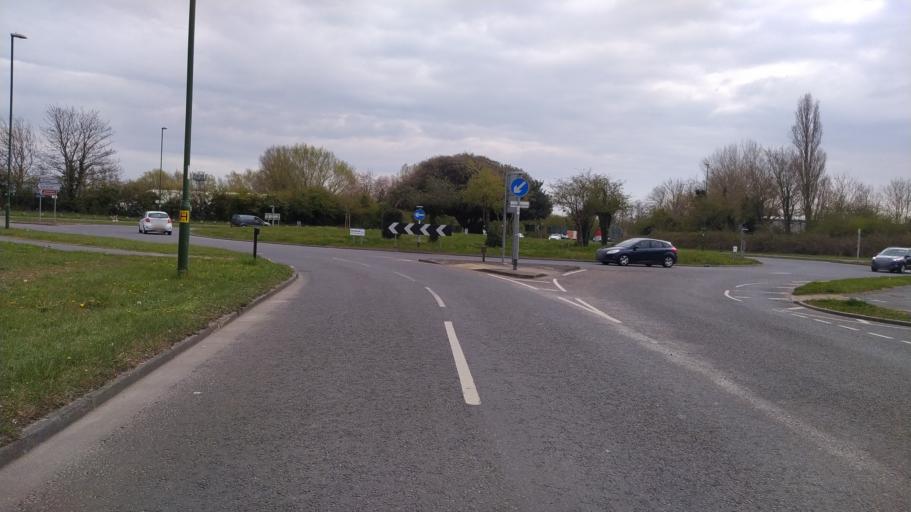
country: GB
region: England
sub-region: West Sussex
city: Chichester
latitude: 50.8468
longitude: -0.7562
